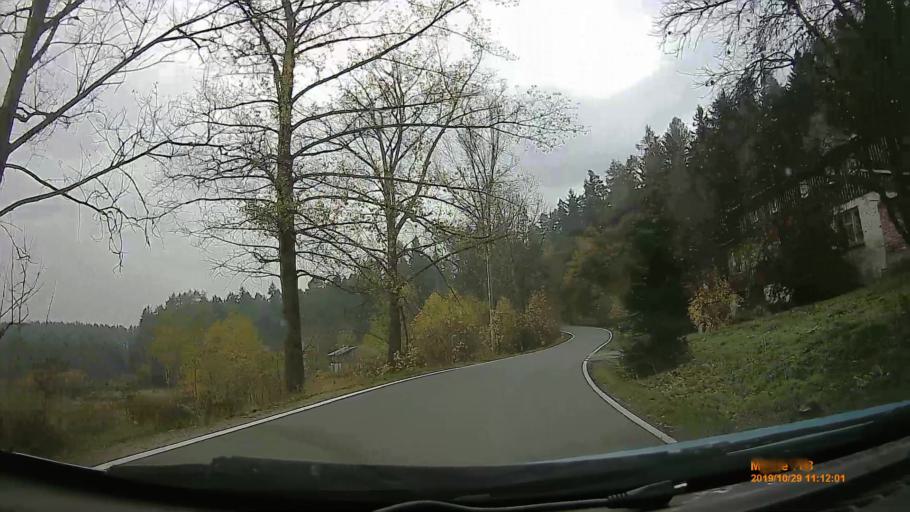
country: PL
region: Lower Silesian Voivodeship
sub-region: Powiat klodzki
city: Polanica-Zdroj
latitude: 50.4305
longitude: 16.5049
